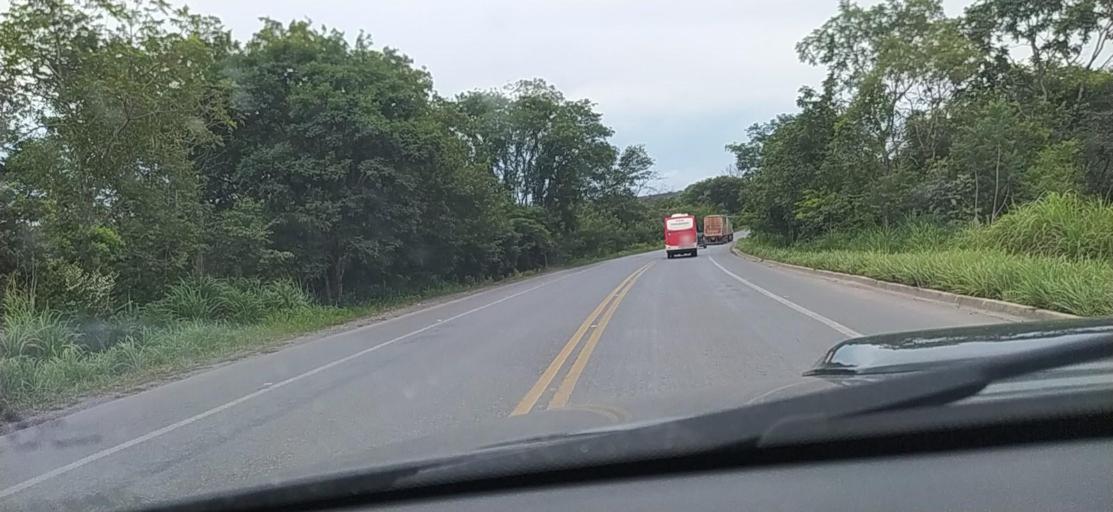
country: BR
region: Minas Gerais
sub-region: Montes Claros
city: Montes Claros
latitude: -16.6650
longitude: -43.7842
